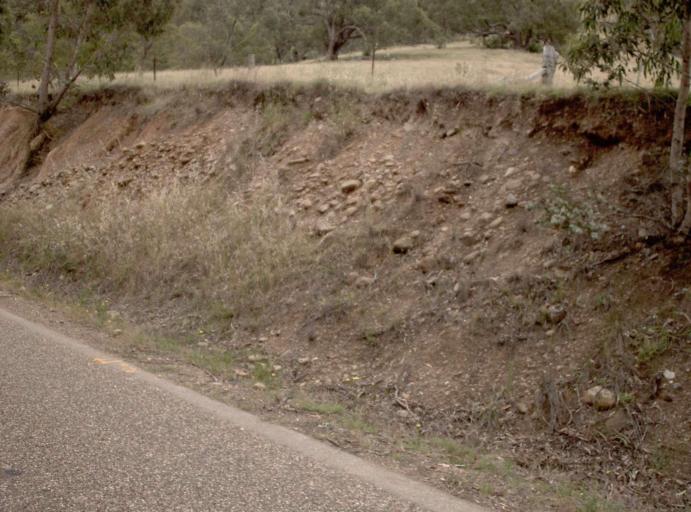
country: AU
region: Victoria
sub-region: East Gippsland
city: Bairnsdale
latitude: -37.5100
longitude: 147.2035
